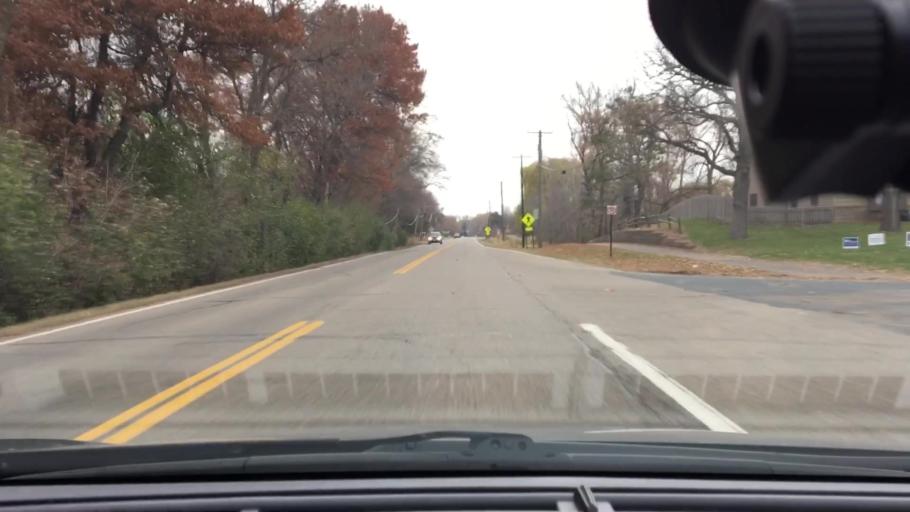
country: US
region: Minnesota
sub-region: Hennepin County
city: Corcoran
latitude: 45.1032
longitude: -93.5120
